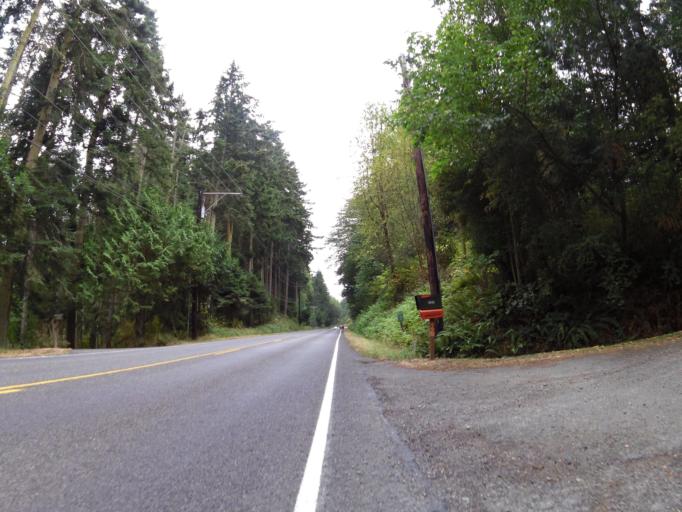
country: US
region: Washington
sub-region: Jefferson County
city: Port Hadlock-Irondale
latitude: 48.0134
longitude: -122.7298
